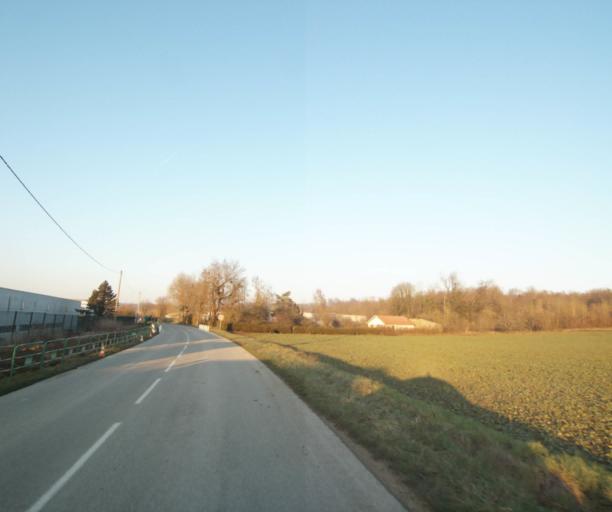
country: FR
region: Champagne-Ardenne
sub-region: Departement de la Haute-Marne
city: Bienville
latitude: 48.5965
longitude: 5.0428
